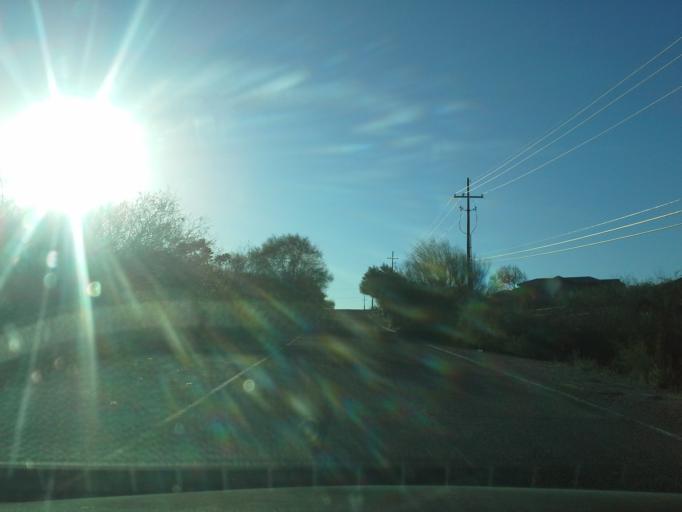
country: US
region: Arizona
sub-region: Pima County
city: South Tucson
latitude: 32.2214
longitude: -111.0218
